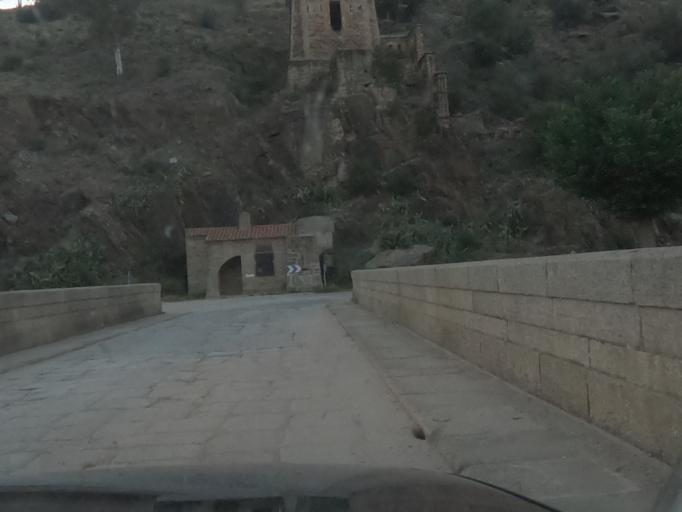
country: ES
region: Extremadura
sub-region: Provincia de Caceres
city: Alcantara
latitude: 39.7229
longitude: -6.8930
